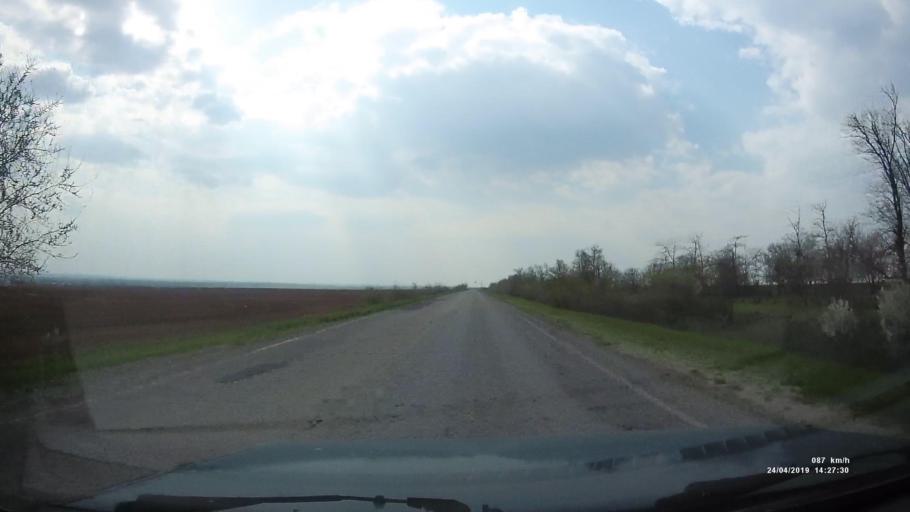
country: RU
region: Kalmykiya
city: Arshan'
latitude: 46.3338
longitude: 44.0421
